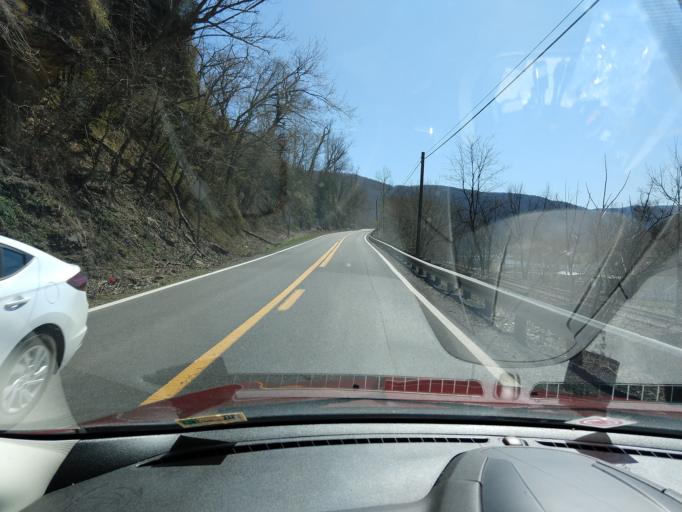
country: US
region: West Virginia
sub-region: Summers County
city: Hinton
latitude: 37.7731
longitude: -80.8910
